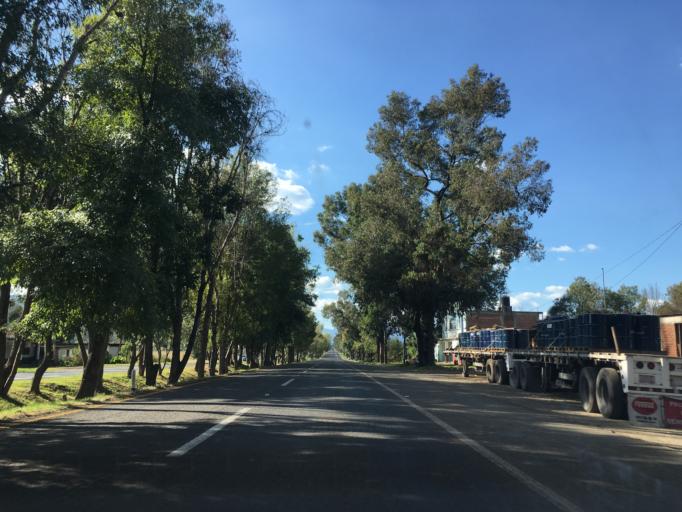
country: MX
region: Michoacan
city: Patzcuaro
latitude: 19.5377
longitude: -101.5746
